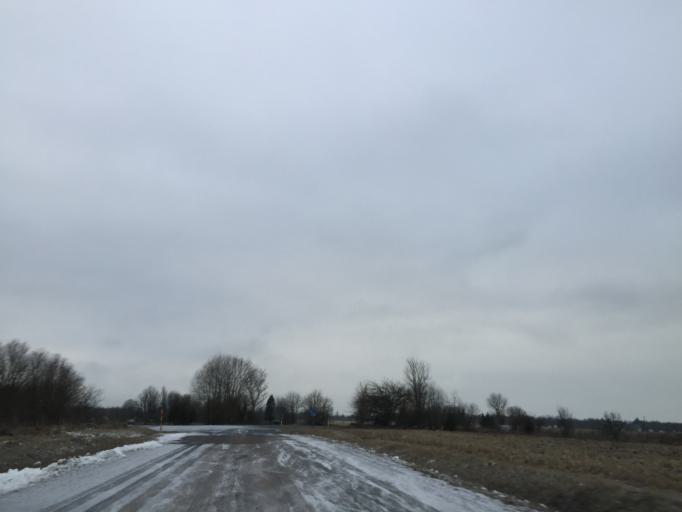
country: EE
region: Saare
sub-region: Orissaare vald
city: Orissaare
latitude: 58.6721
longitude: 23.2065
